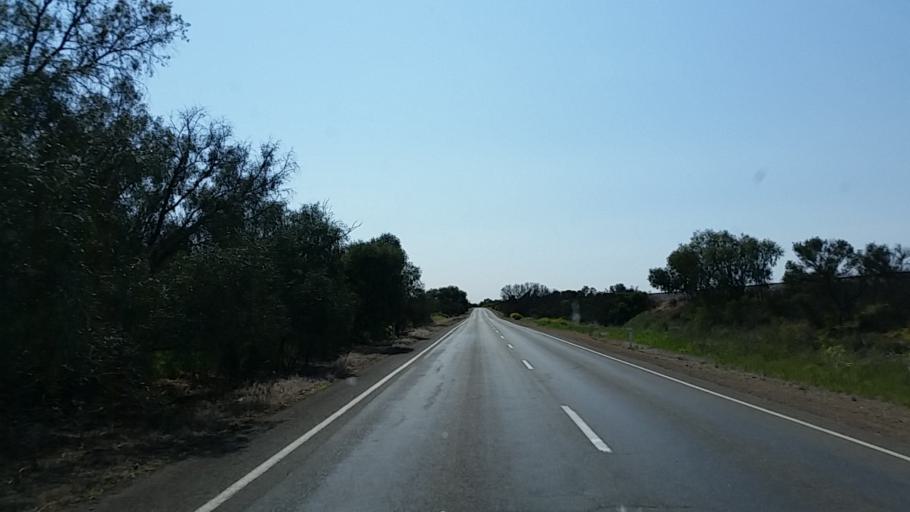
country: AU
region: South Australia
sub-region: Port Pirie City and Dists
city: Crystal Brook
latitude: -33.2380
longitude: 138.3855
